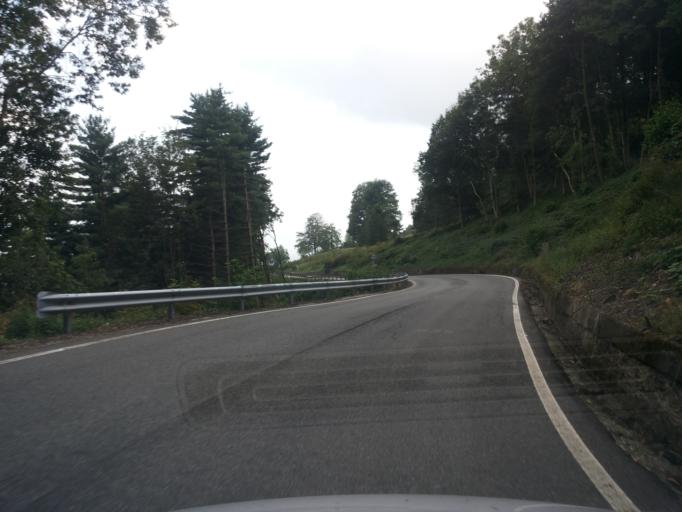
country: IT
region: Piedmont
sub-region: Provincia di Biella
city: Pollone
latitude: 45.6072
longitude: 7.9917
